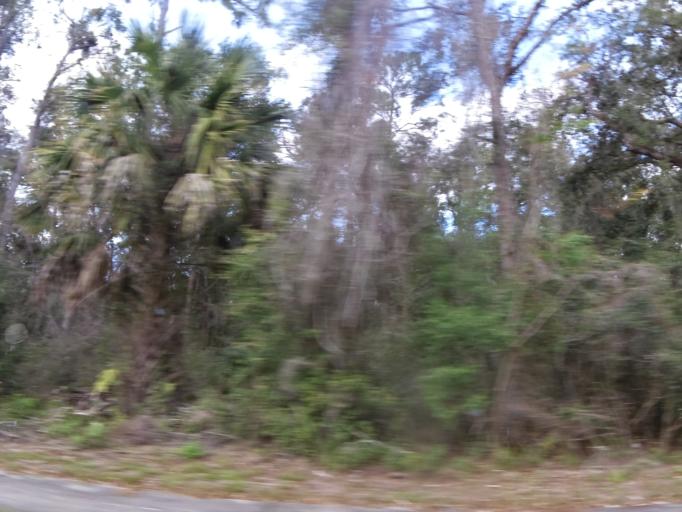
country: US
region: Florida
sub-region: Volusia County
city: Orange City
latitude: 28.9487
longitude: -81.2845
